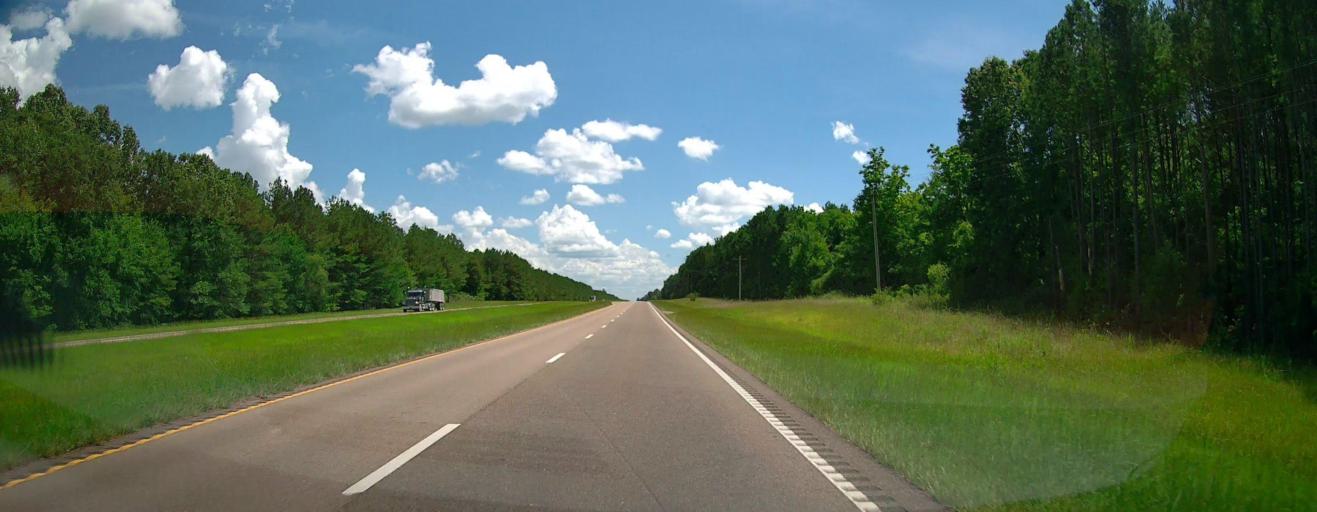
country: US
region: Mississippi
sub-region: Monroe County
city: Aberdeen
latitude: 33.9172
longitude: -88.5962
